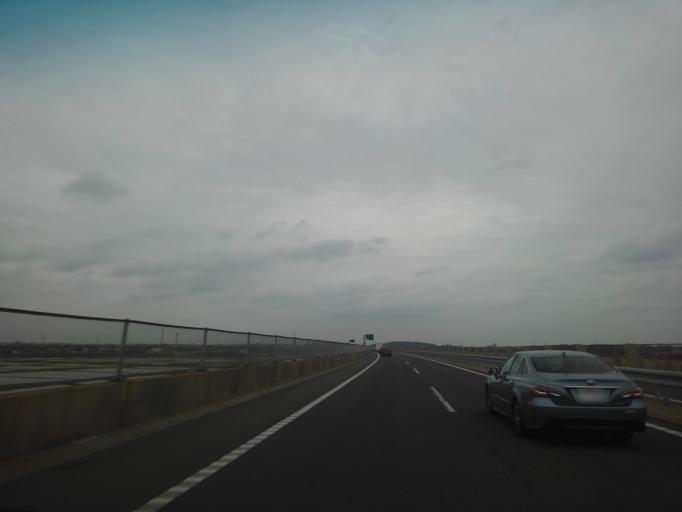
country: JP
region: Chiba
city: Kisarazu
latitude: 35.4030
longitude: 139.9660
